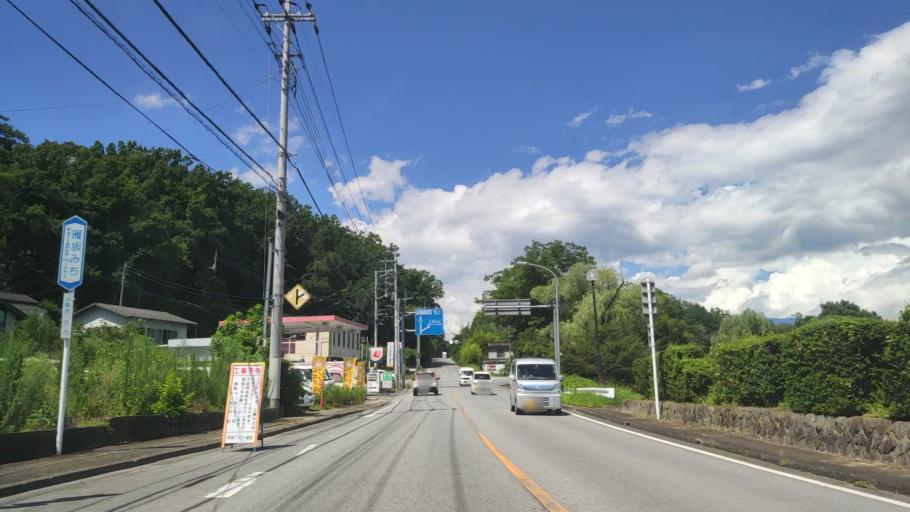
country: JP
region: Yamanashi
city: Enzan
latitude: 35.6943
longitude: 138.6812
